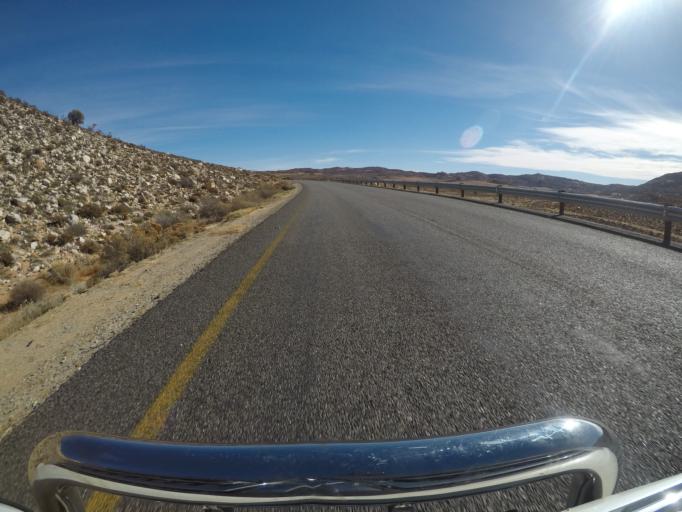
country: ZA
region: Northern Cape
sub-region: Namakwa District Municipality
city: Springbok
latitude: -29.4444
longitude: 17.8394
